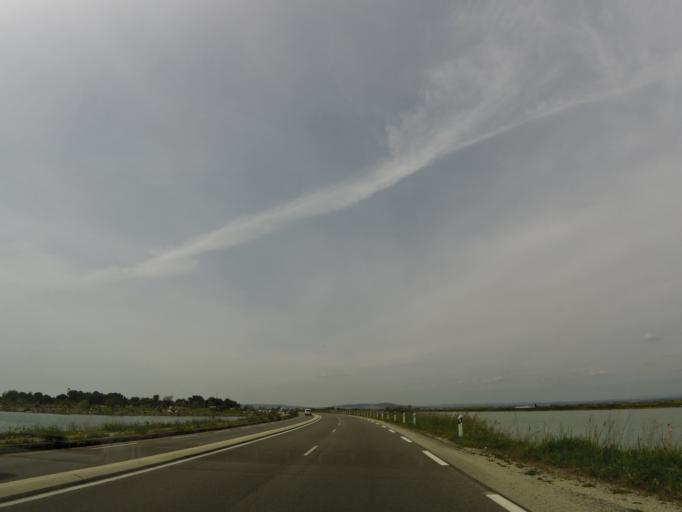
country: FR
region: Languedoc-Roussillon
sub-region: Departement de l'Herault
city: Palavas-les-Flots
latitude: 43.5357
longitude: 3.9330
